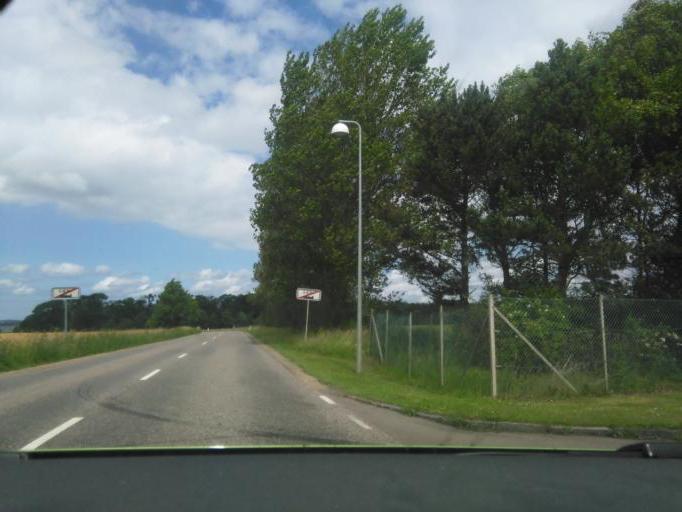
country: DK
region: Zealand
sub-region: Kalundborg Kommune
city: Hong
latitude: 55.5504
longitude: 11.3090
